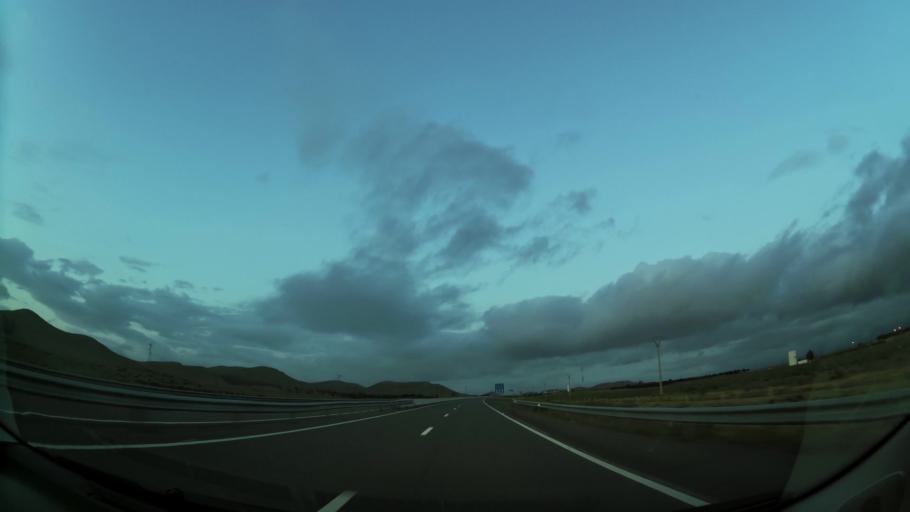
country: MA
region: Oriental
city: El Aioun
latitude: 34.6172
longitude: -2.4512
